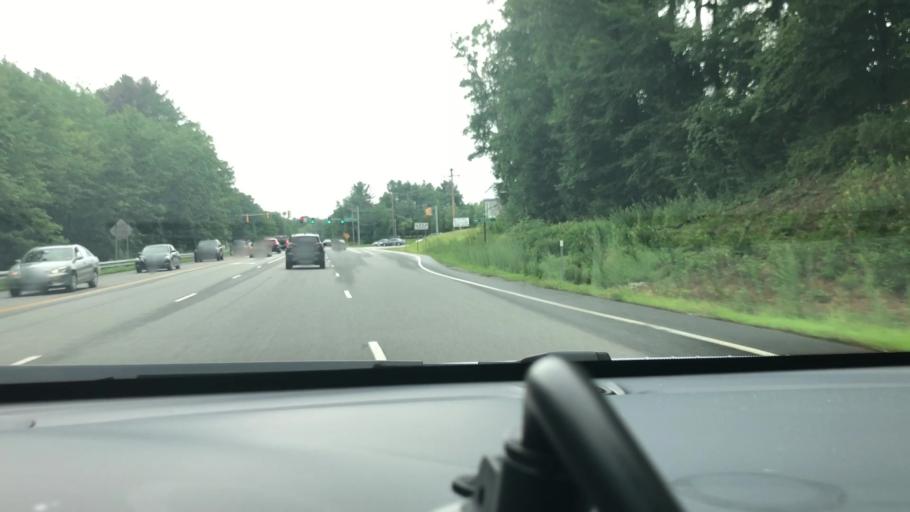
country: US
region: New Hampshire
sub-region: Hillsborough County
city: Bedford
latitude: 42.9678
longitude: -71.5072
